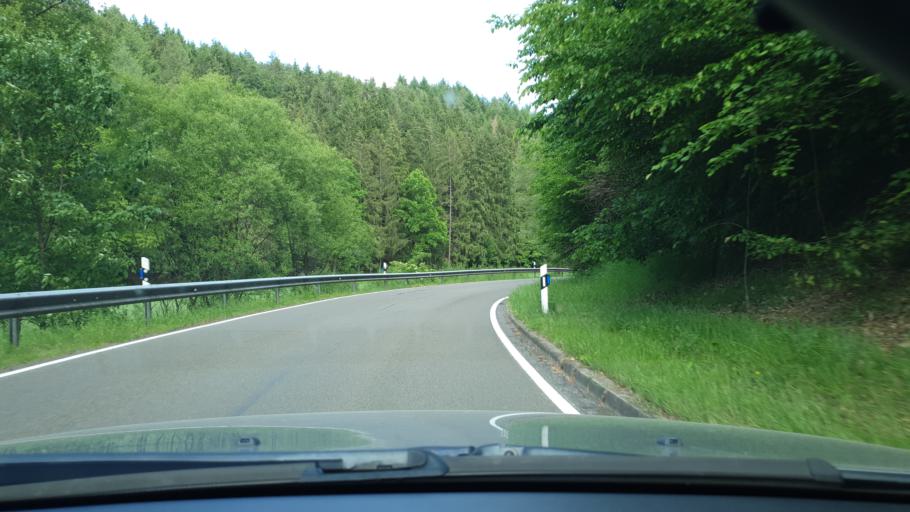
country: DE
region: Rheinland-Pfalz
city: Battweiler
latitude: 49.2830
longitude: 7.4826
